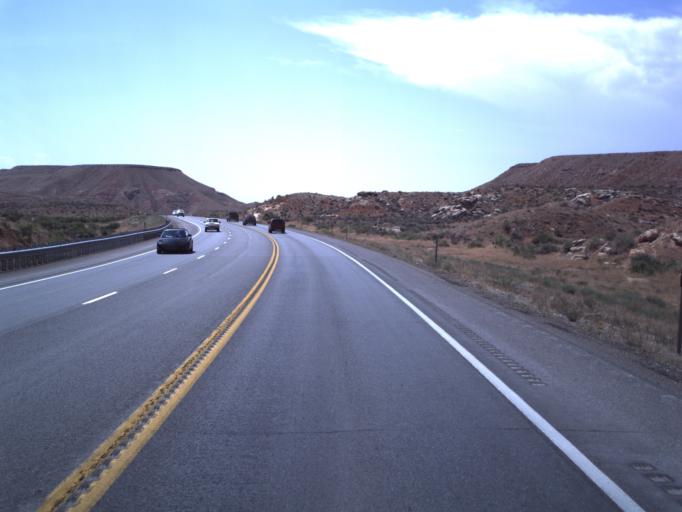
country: US
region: Utah
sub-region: Uintah County
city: Maeser
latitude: 40.3629
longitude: -109.6165
